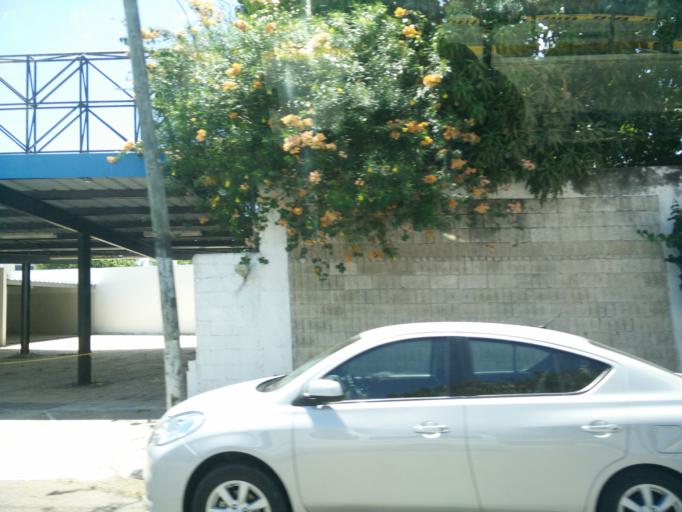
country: MX
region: Yucatan
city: Merida
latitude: 21.0222
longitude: -89.6212
